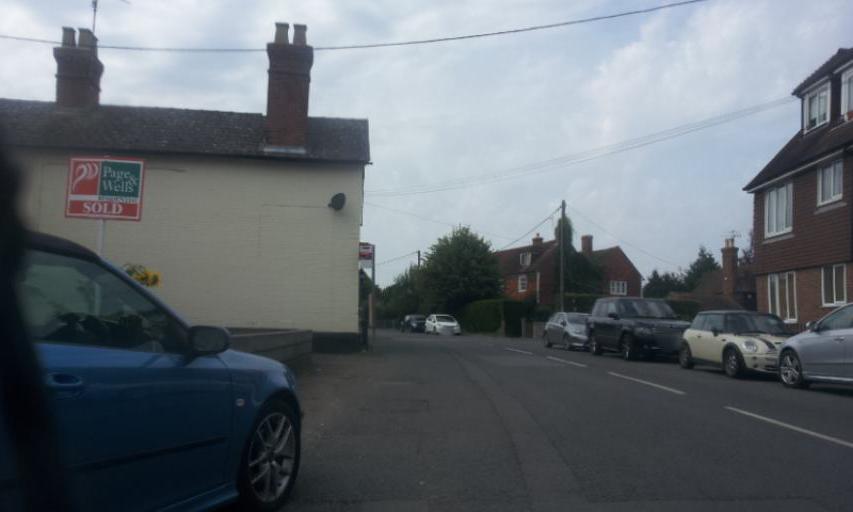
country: GB
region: England
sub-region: Kent
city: Yalding
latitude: 51.2235
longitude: 0.4287
